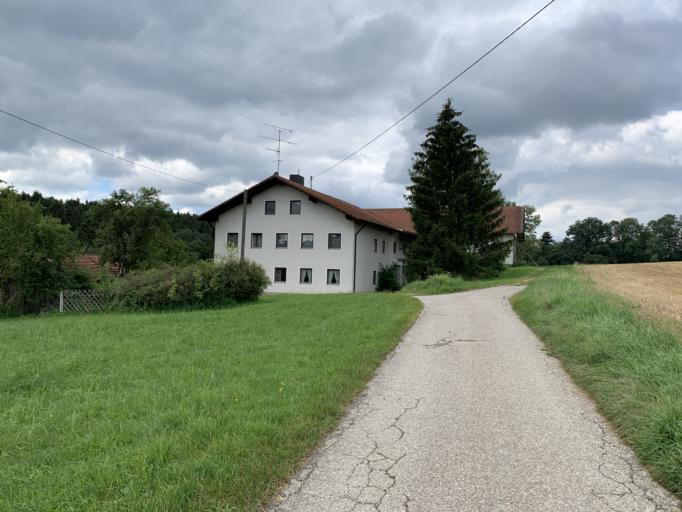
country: DE
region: Bavaria
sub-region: Upper Bavaria
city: Buch am Buchrain
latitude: 48.1861
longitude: 12.0244
